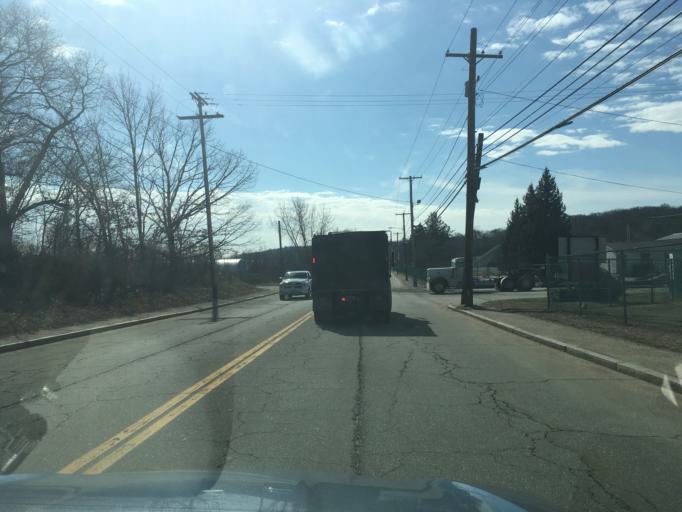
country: US
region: Rhode Island
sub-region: Providence County
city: Cranston
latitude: 41.7635
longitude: -71.4837
